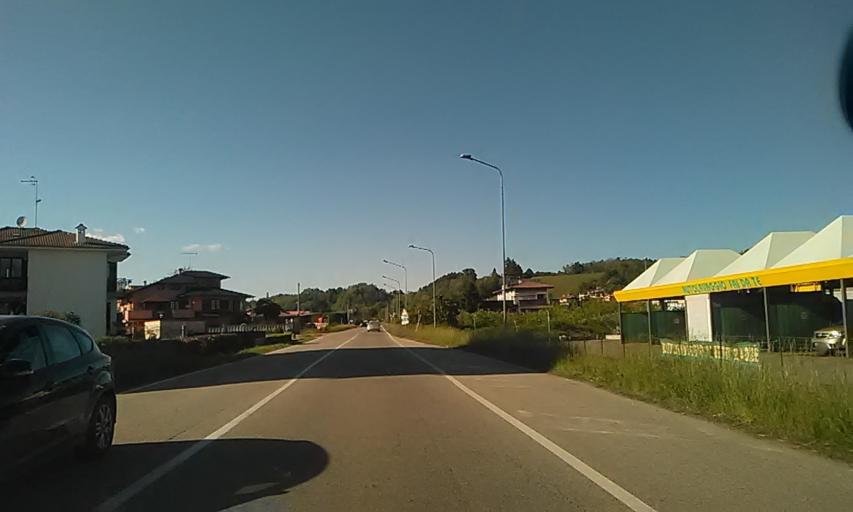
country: IT
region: Piedmont
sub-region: Provincia di Novara
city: Ghemme
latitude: 45.5922
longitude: 8.4267
